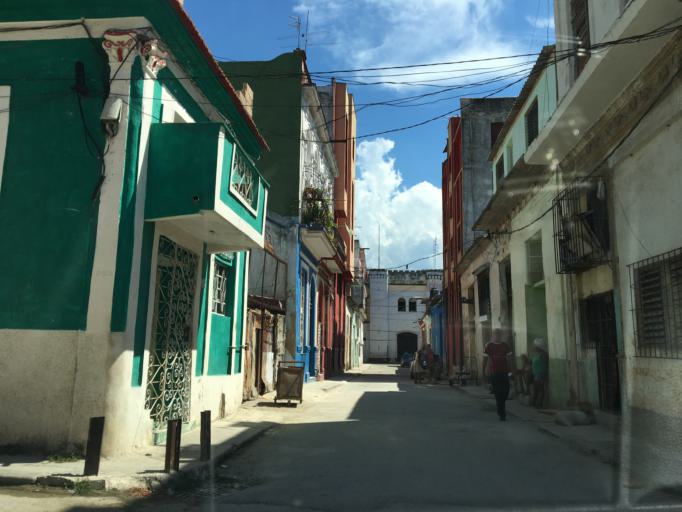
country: CU
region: La Habana
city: La Habana Vieja
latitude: 23.1272
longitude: -82.3577
